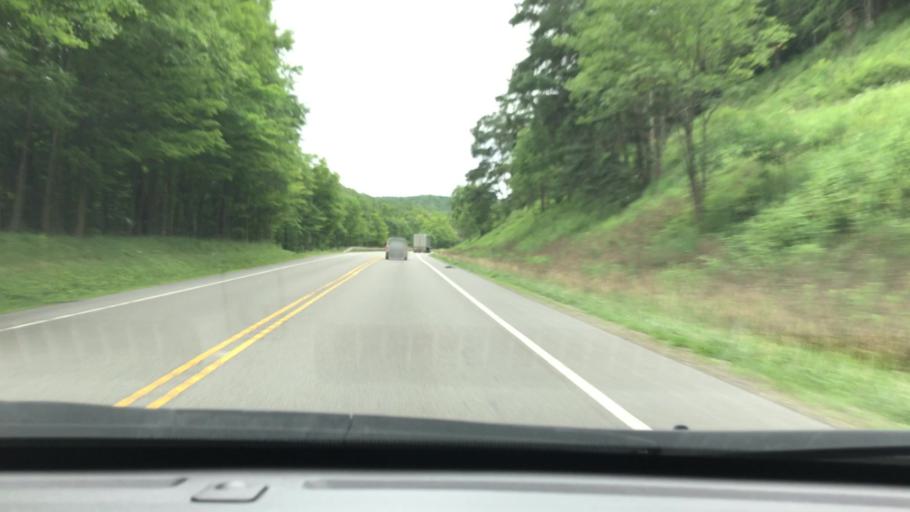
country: US
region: Pennsylvania
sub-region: McKean County
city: Kane
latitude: 41.6748
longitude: -78.6834
